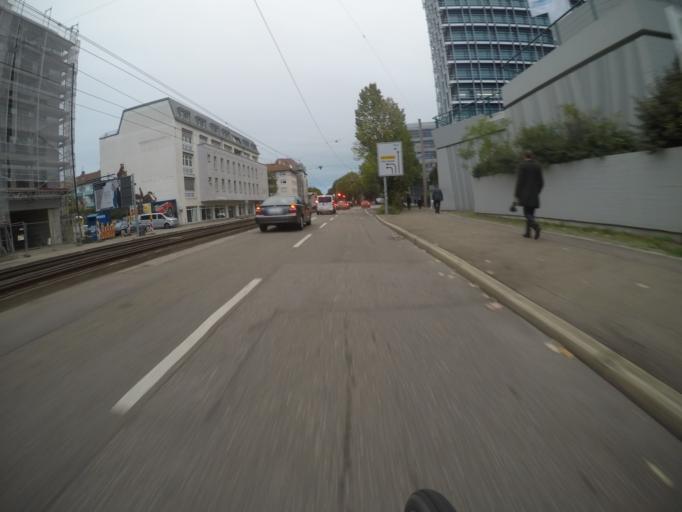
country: DE
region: Baden-Wuerttemberg
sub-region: Regierungsbezirk Stuttgart
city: Stuttgart-Ost
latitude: 48.7935
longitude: 9.2029
